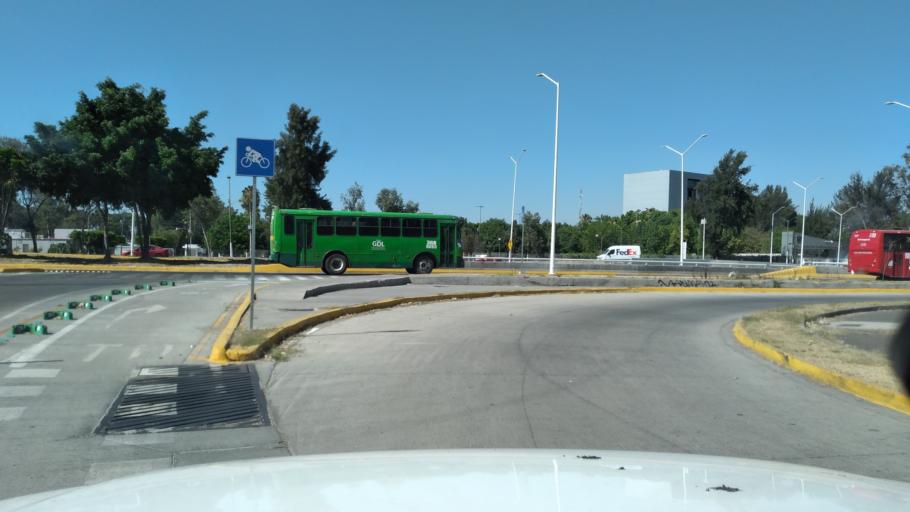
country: MX
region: Jalisco
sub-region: Zapopan
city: Zapopan
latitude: 20.7389
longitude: -103.3830
